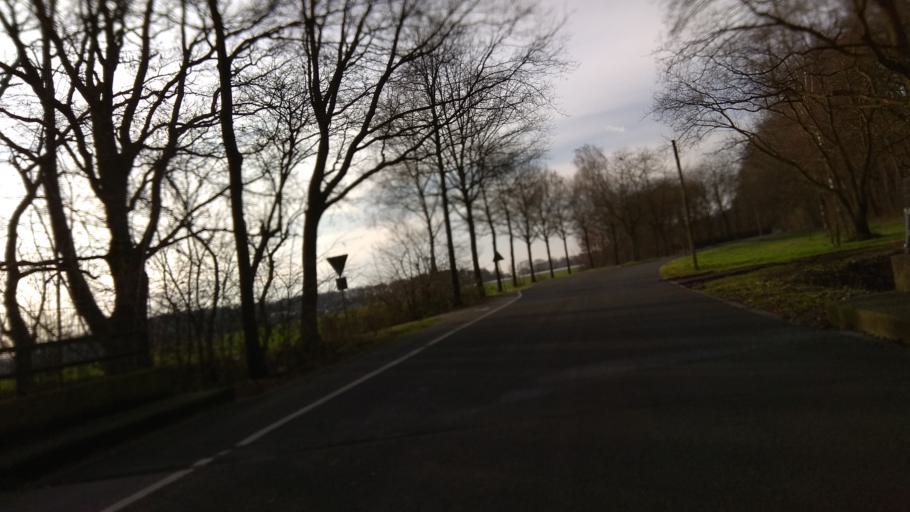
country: DE
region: North Rhine-Westphalia
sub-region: Regierungsbezirk Munster
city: Klein Reken
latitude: 51.7355
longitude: 7.0341
